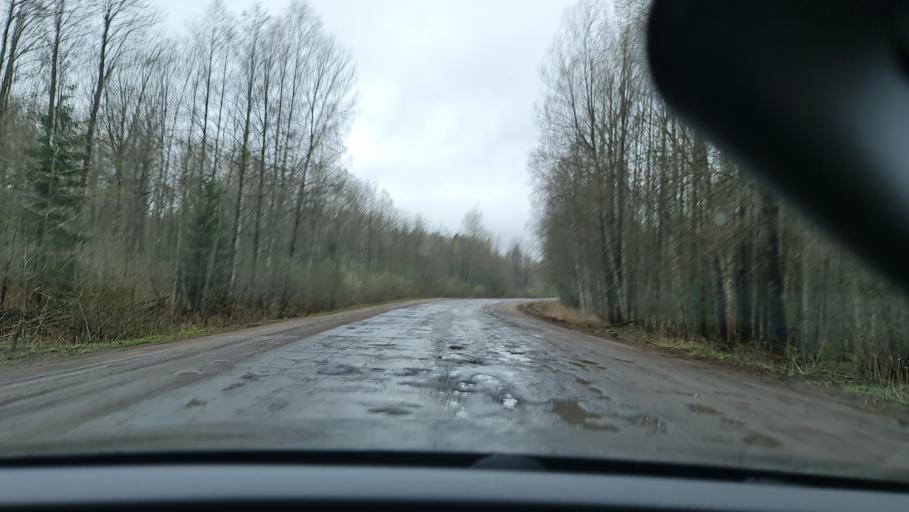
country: RU
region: Novgorod
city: Demyansk
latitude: 57.6762
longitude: 32.5521
